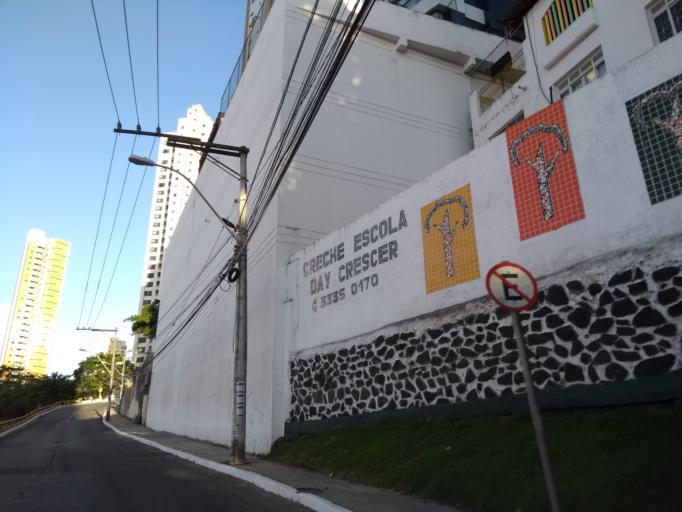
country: BR
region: Bahia
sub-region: Salvador
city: Salvador
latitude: -12.9999
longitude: -38.4896
